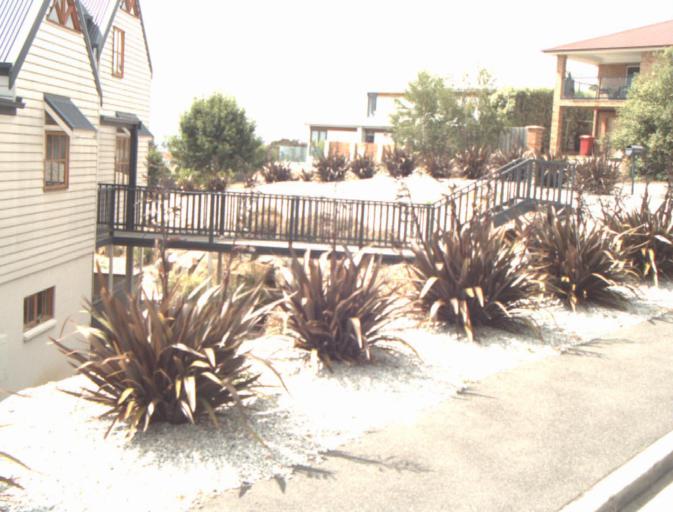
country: AU
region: Tasmania
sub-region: Launceston
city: Summerhill
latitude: -41.4672
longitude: 147.1478
